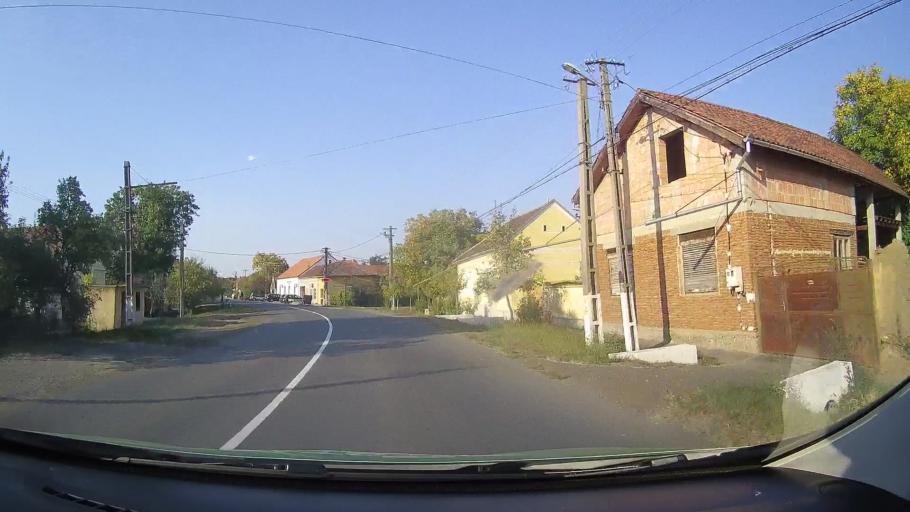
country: RO
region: Arad
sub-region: Comuna Ghioroc
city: Ghioroc
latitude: 46.1376
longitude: 21.6048
